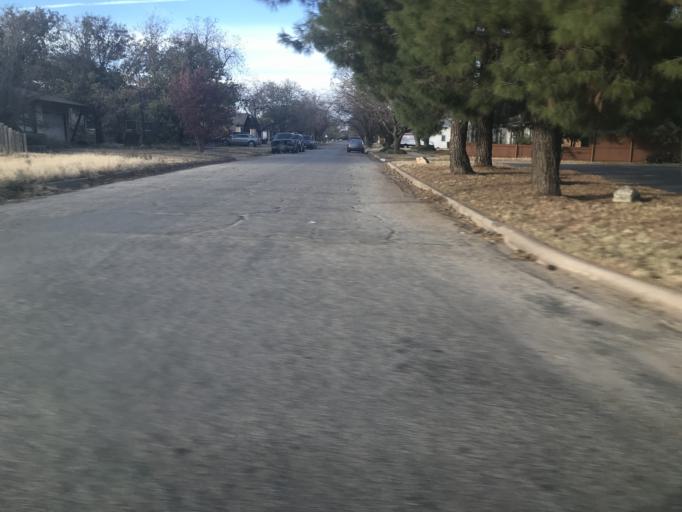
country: US
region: Texas
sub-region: Taylor County
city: Abilene
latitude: 32.4322
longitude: -99.7420
